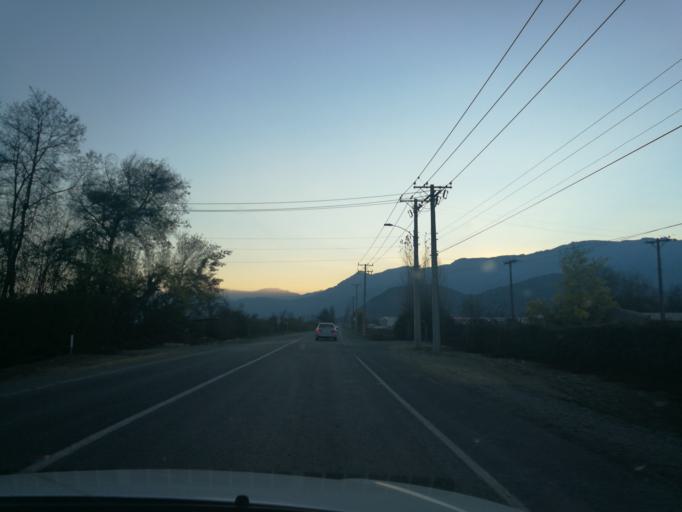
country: CL
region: O'Higgins
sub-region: Provincia de Cachapoal
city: Graneros
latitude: -34.0391
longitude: -70.6953
